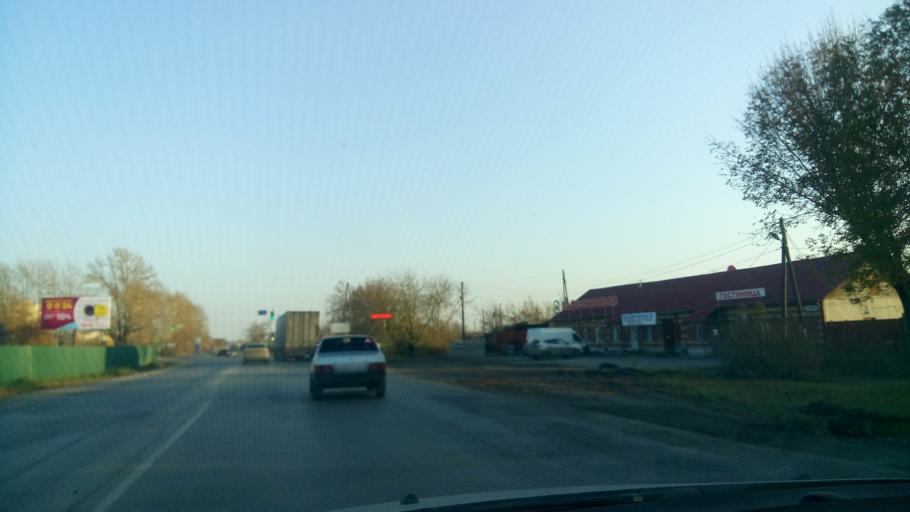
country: RU
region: Sverdlovsk
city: Bogdanovich
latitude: 56.7757
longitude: 62.0321
